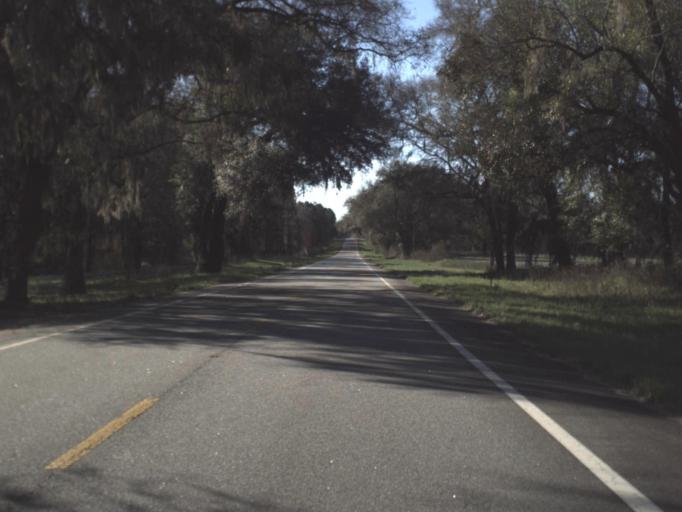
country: US
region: Georgia
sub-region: Brooks County
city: Quitman
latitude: 30.6057
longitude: -83.6456
